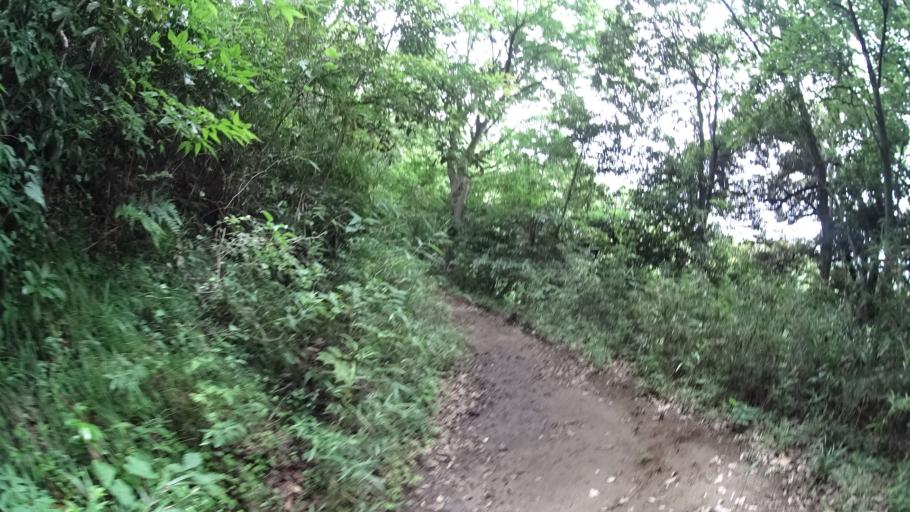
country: JP
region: Kanagawa
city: Zushi
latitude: 35.3376
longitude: 139.5881
